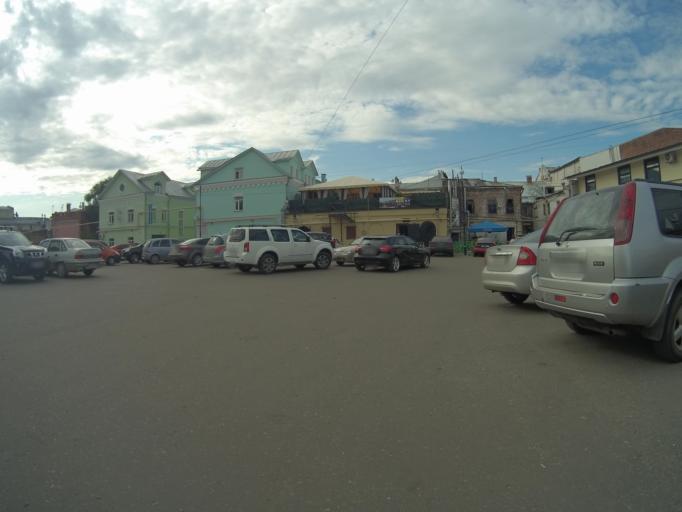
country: RU
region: Vladimir
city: Vladimir
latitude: 56.1268
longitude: 40.4011
